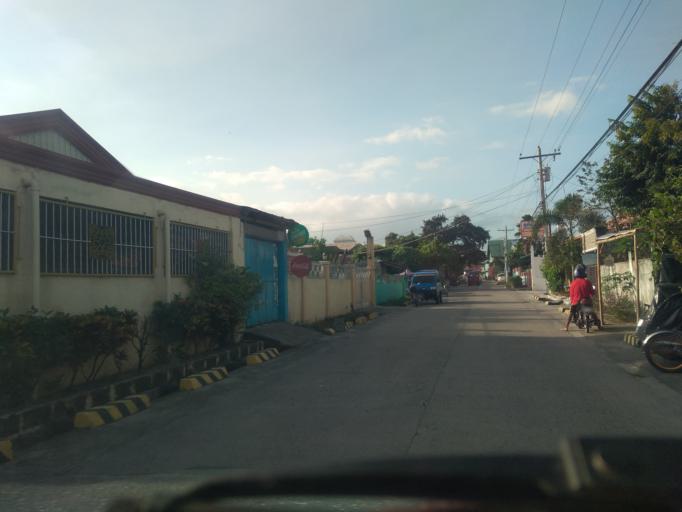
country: PH
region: Central Luzon
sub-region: Province of Pampanga
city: Bulaon
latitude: 15.1017
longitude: 120.6777
